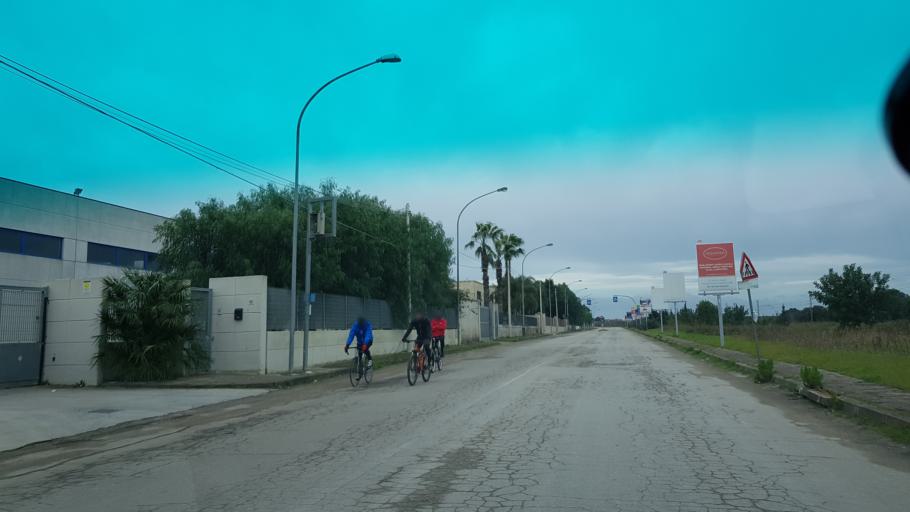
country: IT
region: Apulia
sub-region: Provincia di Brindisi
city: Mesagne
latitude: 40.5747
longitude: 17.8246
